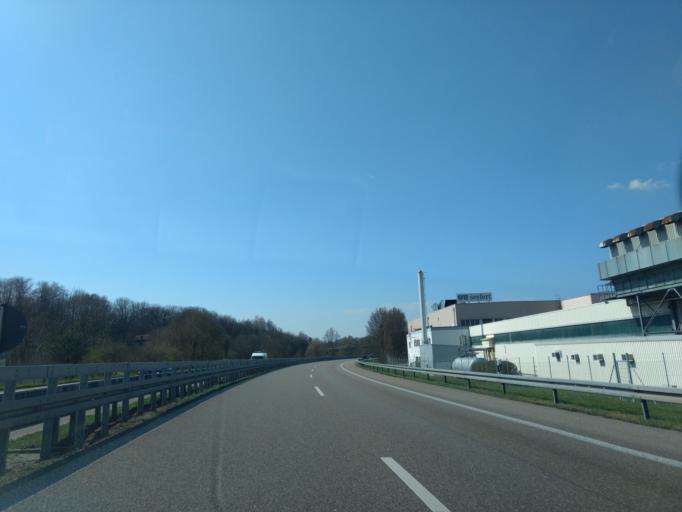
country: DE
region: Baden-Wuerttemberg
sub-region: Regierungsbezirk Stuttgart
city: Reichenbach an der Fils
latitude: 48.7070
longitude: 9.4733
